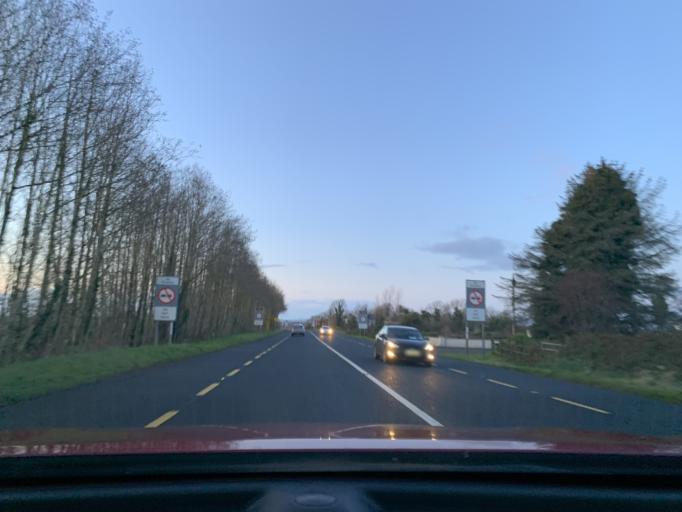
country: IE
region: Connaught
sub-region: County Leitrim
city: Carrick-on-Shannon
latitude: 53.8980
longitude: -7.9532
